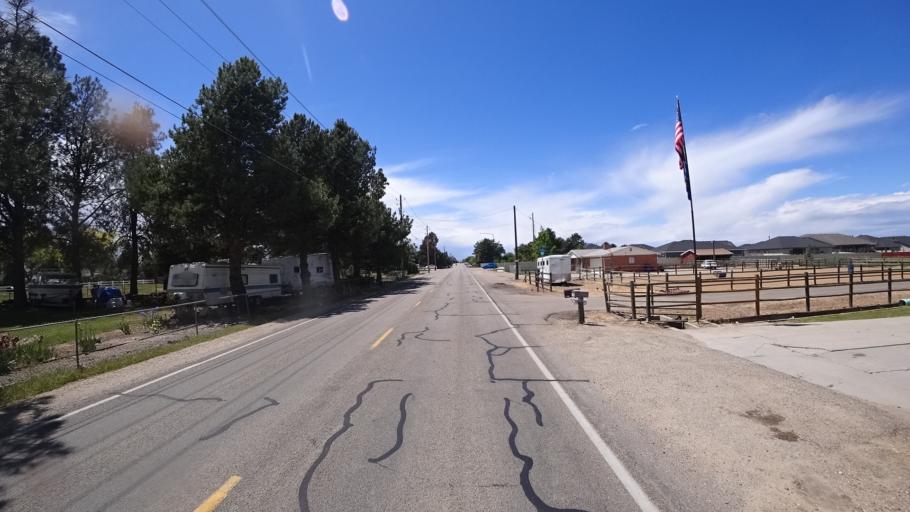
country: US
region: Idaho
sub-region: Ada County
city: Meridian
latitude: 43.5758
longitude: -116.3450
